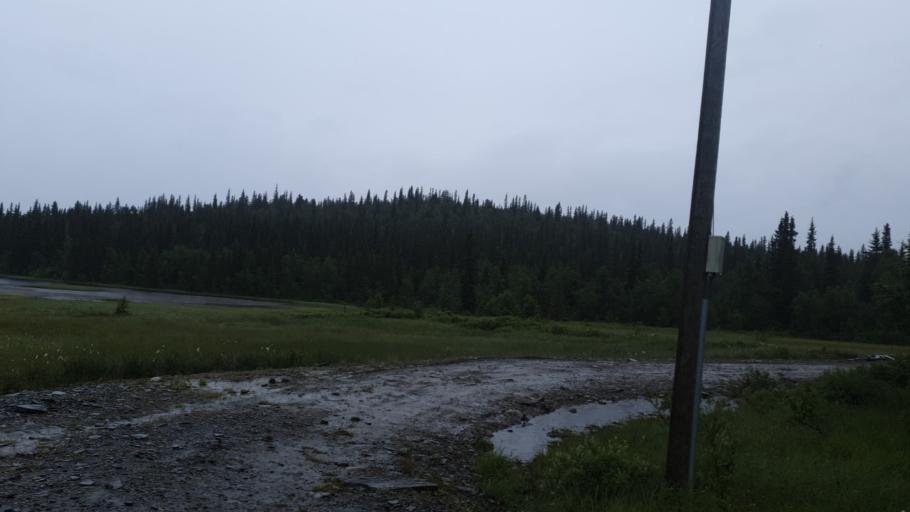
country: NO
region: Oppland
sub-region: Vestre Slidre
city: Slidre
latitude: 61.2334
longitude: 8.9181
